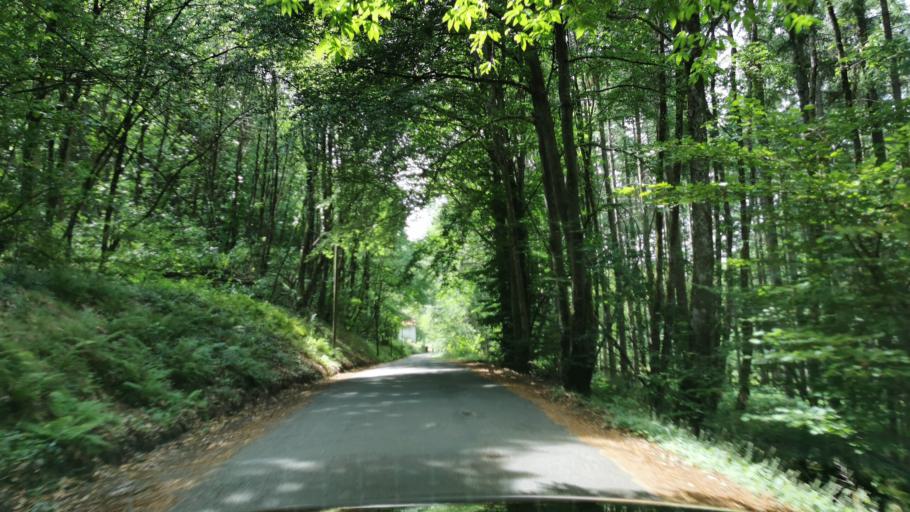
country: FR
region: Bourgogne
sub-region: Departement de Saone-et-Loire
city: Etang-sur-Arroux
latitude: 46.8129
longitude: 4.2628
